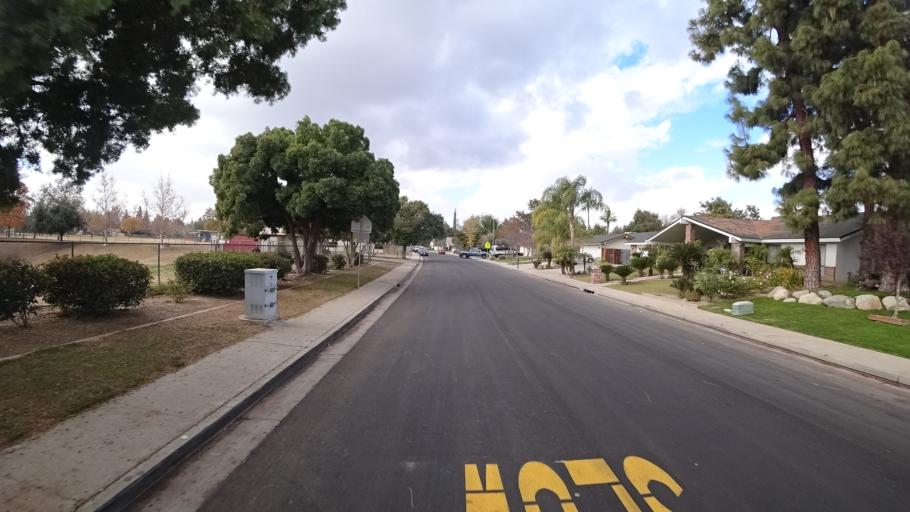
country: US
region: California
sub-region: Kern County
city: Greenacres
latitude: 35.3499
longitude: -119.0869
